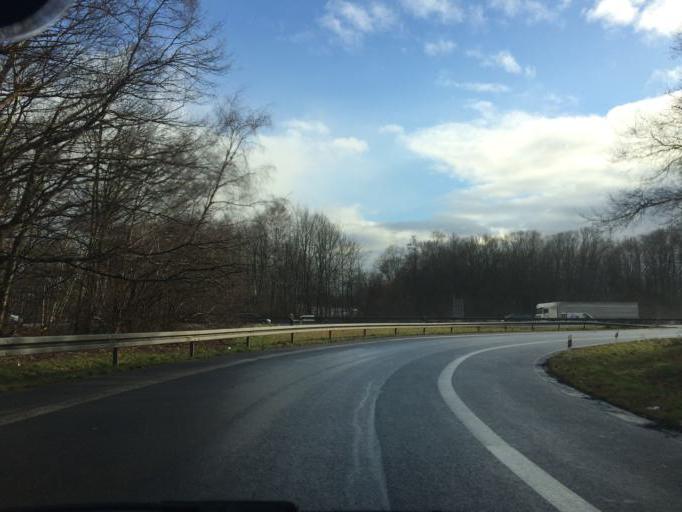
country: DE
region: North Rhine-Westphalia
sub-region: Regierungsbezirk Munster
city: Recklinghausen
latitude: 51.5847
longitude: 7.1908
